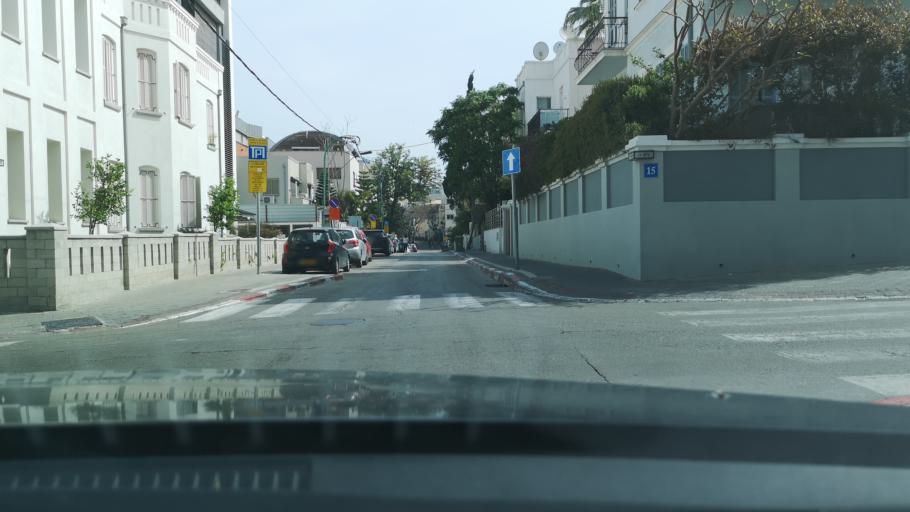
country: IL
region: Tel Aviv
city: Tel Aviv
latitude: 32.0660
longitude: 34.7686
